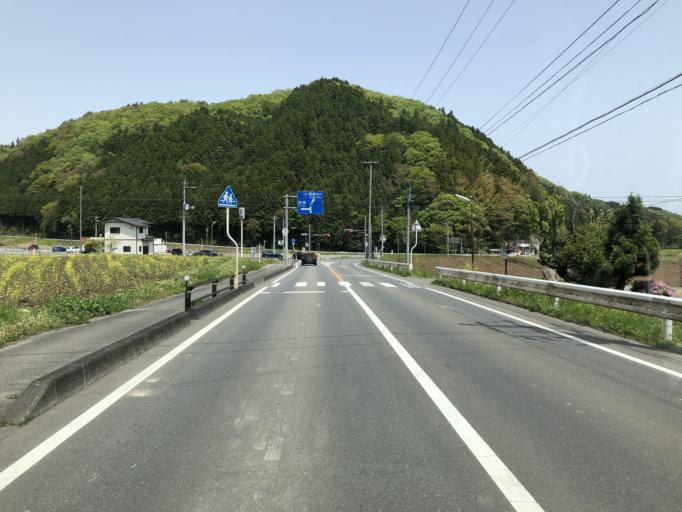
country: JP
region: Fukushima
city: Ishikawa
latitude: 37.0252
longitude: 140.3581
